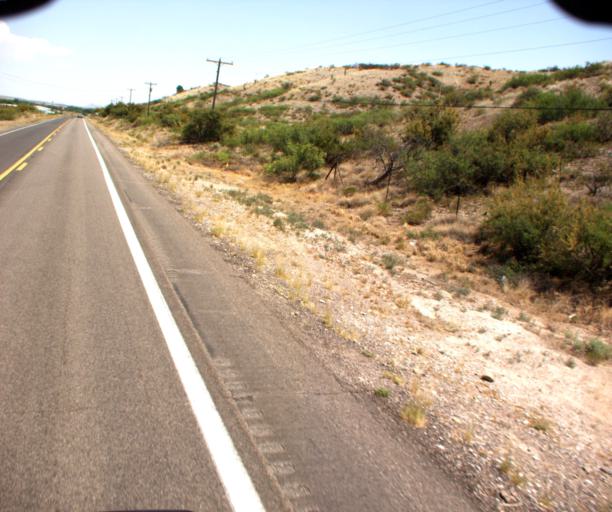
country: US
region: Arizona
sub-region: Greenlee County
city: Clifton
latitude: 32.7338
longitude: -109.1207
